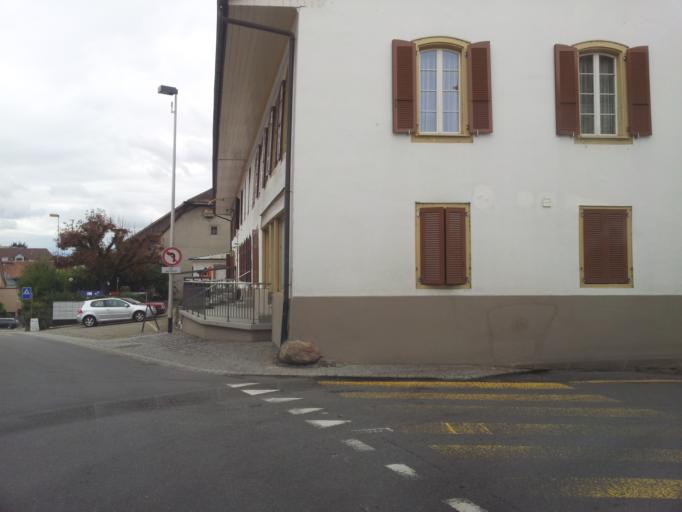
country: CH
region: Fribourg
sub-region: See District
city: Kerzers
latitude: 46.9762
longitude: 7.1957
